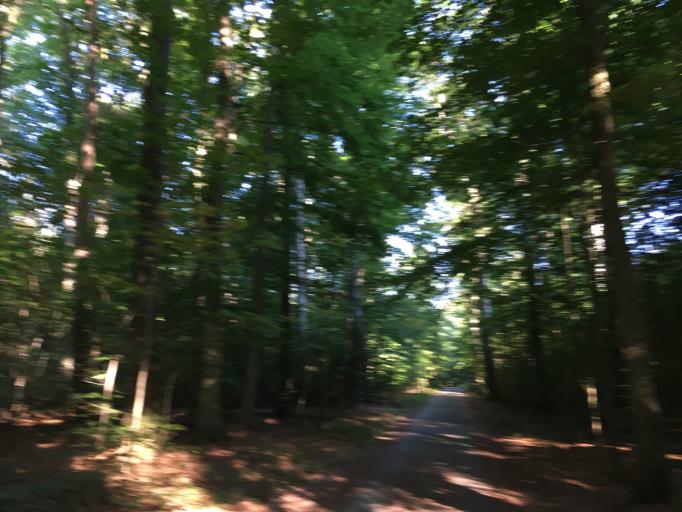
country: DE
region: Hesse
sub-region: Regierungsbezirk Darmstadt
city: Neu Isenburg
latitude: 50.0835
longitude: 8.7147
